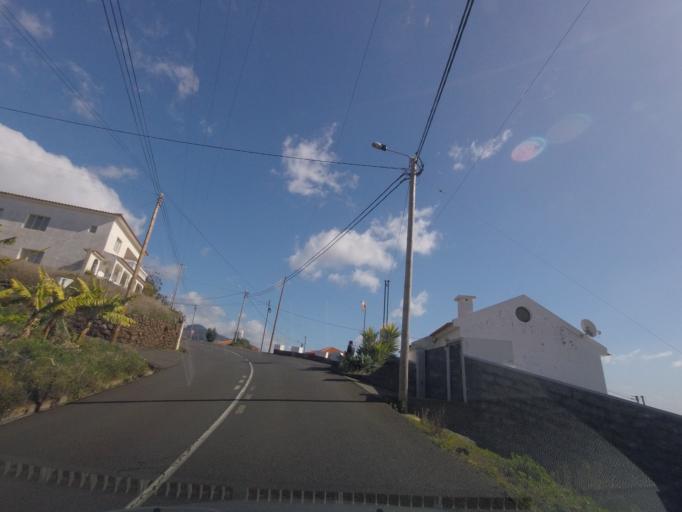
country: PT
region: Madeira
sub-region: Calheta
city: Estreito da Calheta
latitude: 32.7329
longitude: -17.1957
